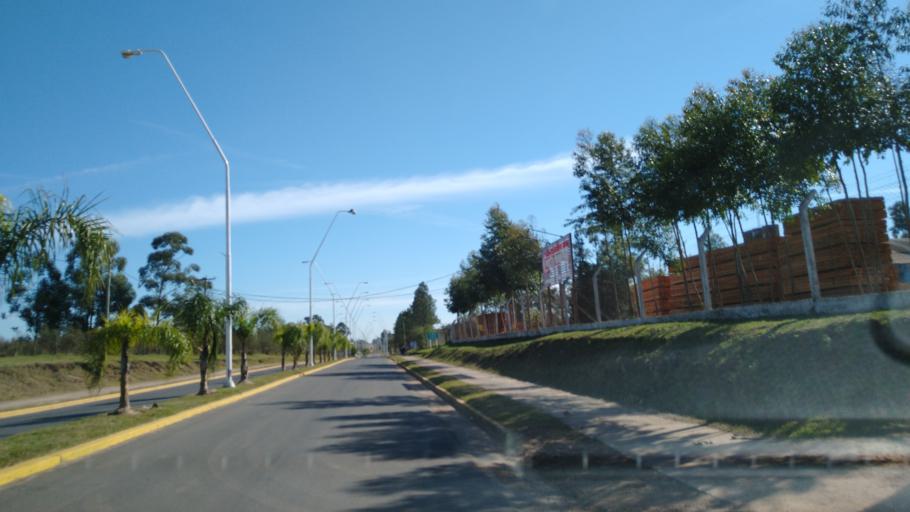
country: AR
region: Entre Rios
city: Chajari
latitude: -30.7480
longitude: -58.0115
